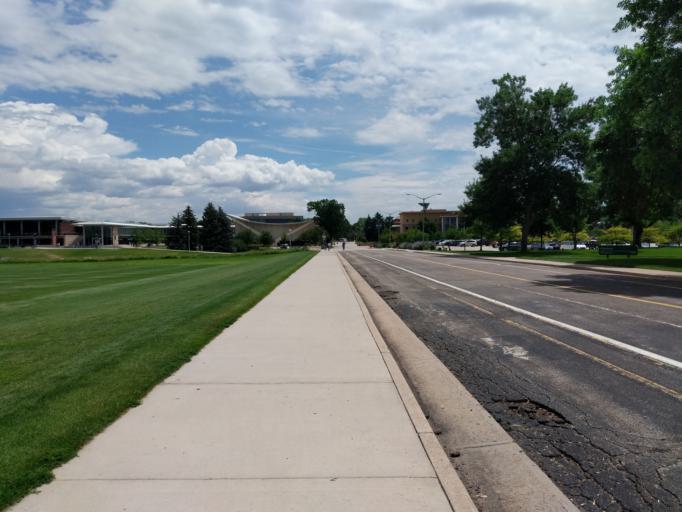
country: US
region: Colorado
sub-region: Larimer County
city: Fort Collins
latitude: 40.5738
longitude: -105.0878
